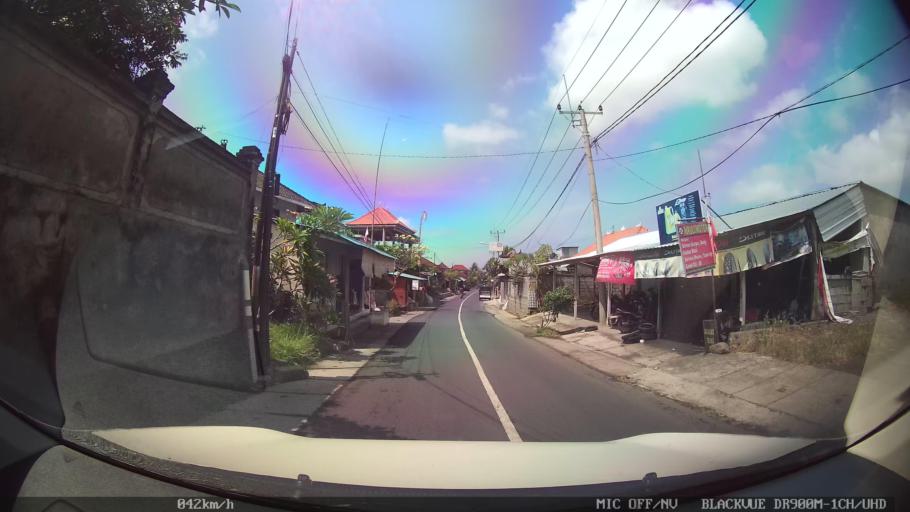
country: ID
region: Bali
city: Banjar Pasekan
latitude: -8.6006
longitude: 115.2915
